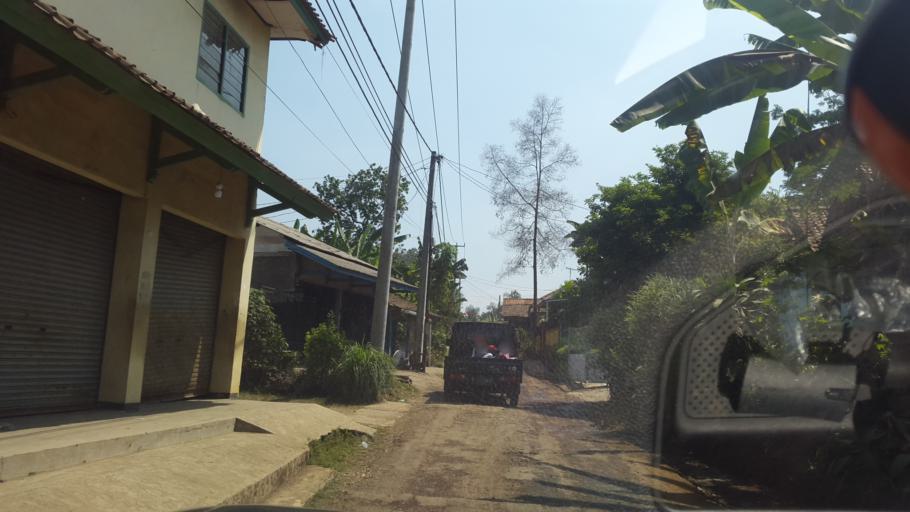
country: ID
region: West Java
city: Cicurug
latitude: -6.8583
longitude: 106.8008
